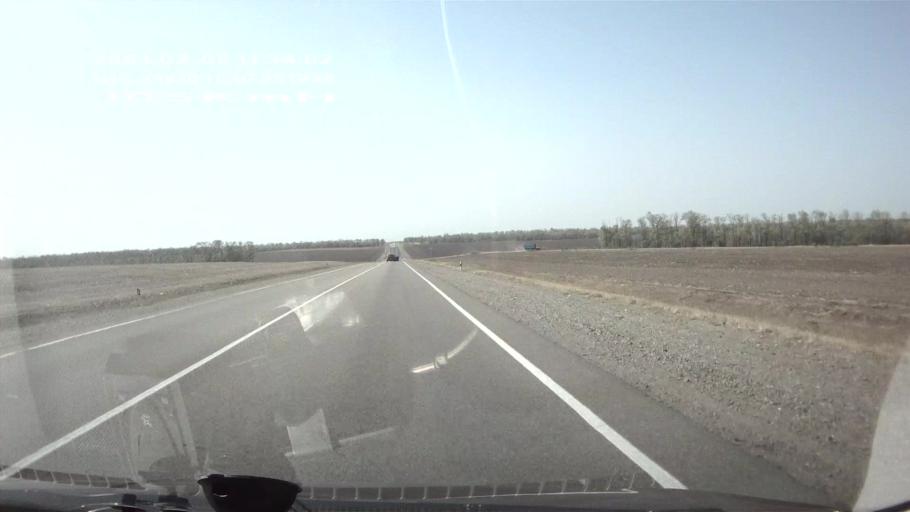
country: RU
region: Krasnodarskiy
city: Kazanskaya
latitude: 45.4437
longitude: 40.3511
